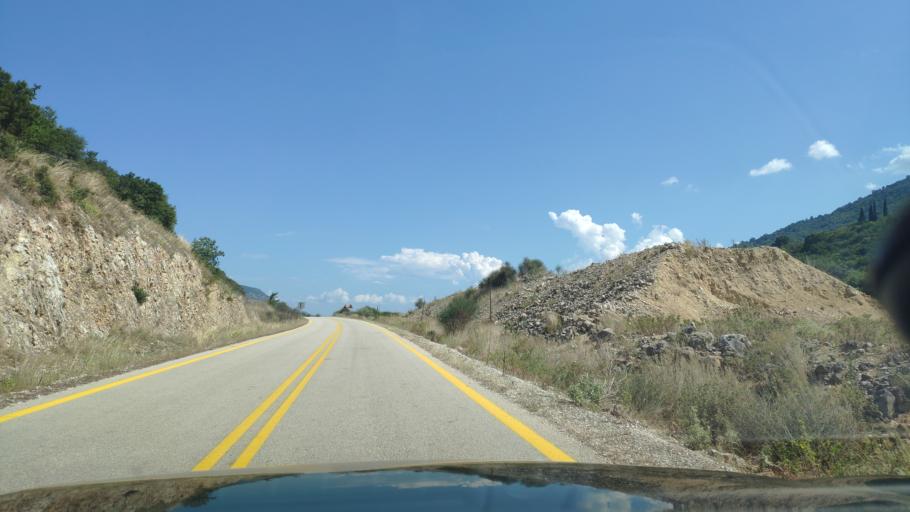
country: GR
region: West Greece
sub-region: Nomos Aitolias kai Akarnanias
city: Katouna
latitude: 38.8551
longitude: 21.0877
